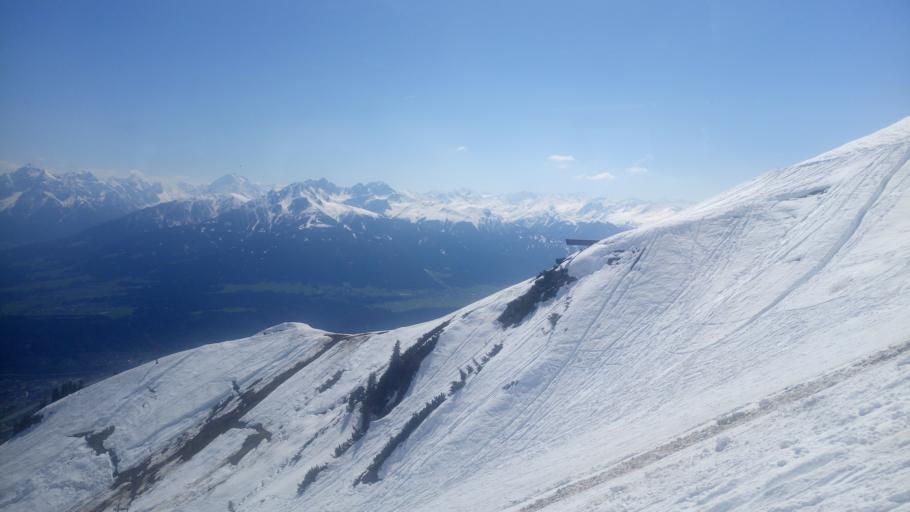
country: AT
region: Tyrol
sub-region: Innsbruck Stadt
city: Innsbruck
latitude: 47.3063
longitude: 11.3800
